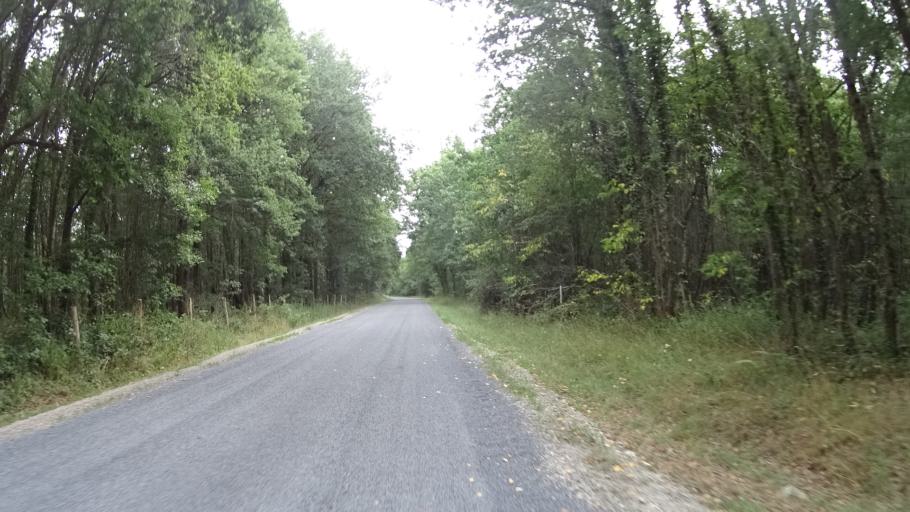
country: FR
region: Centre
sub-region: Departement du Loiret
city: Lorris
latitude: 47.9385
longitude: 2.5610
